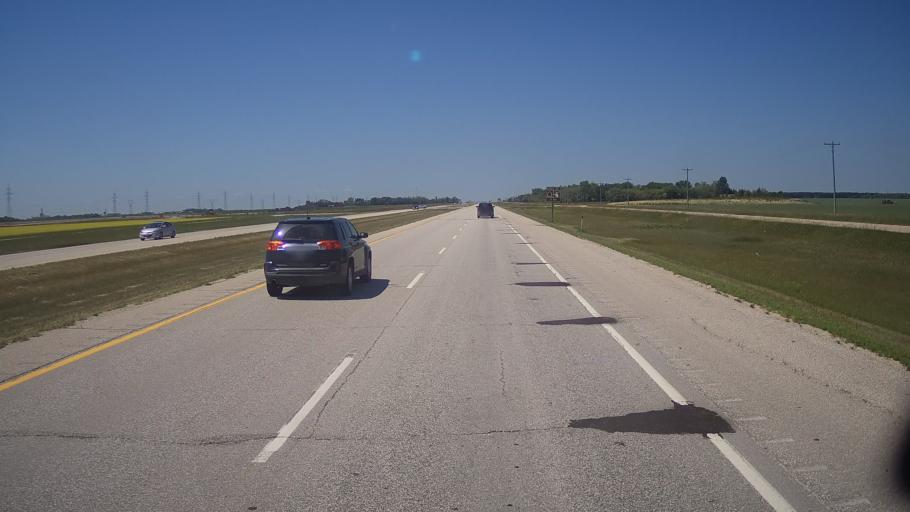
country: CA
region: Manitoba
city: Winnipeg
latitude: 49.9900
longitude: -97.2483
